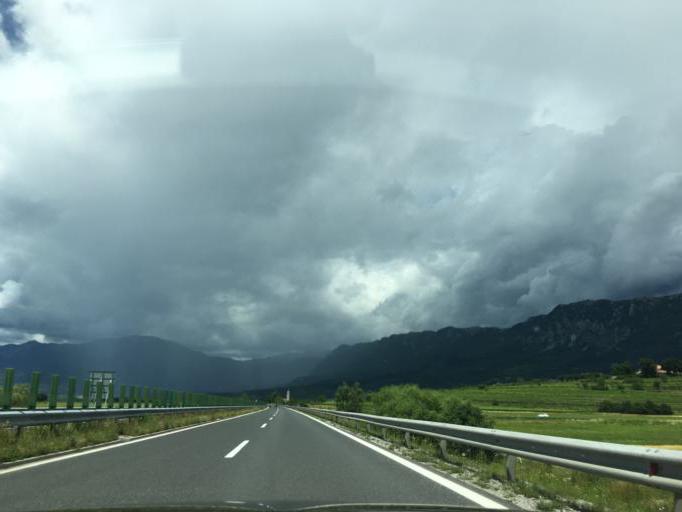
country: SI
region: Vipava
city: Vipava
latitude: 45.8494
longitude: 13.9480
